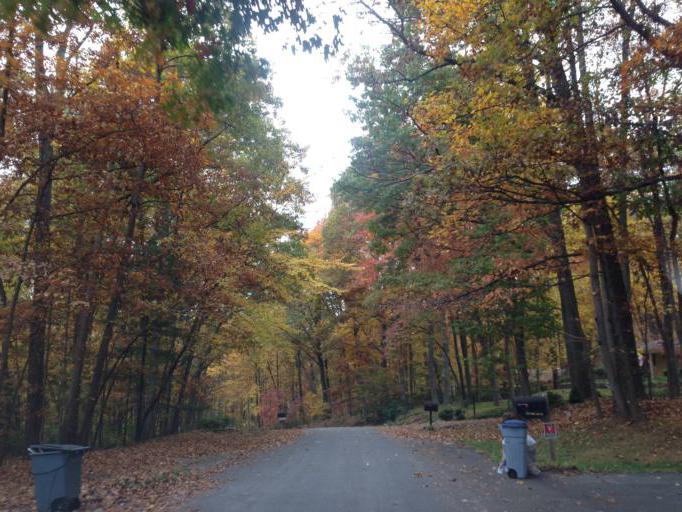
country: US
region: Maryland
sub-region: Howard County
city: Highland
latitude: 39.2755
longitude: -76.9392
